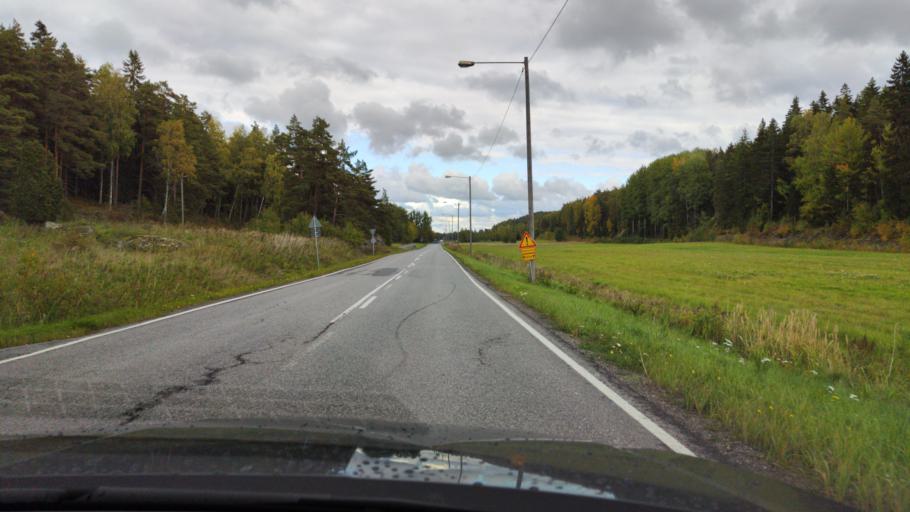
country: FI
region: Varsinais-Suomi
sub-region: Turku
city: Raisio
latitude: 60.3587
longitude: 22.1775
